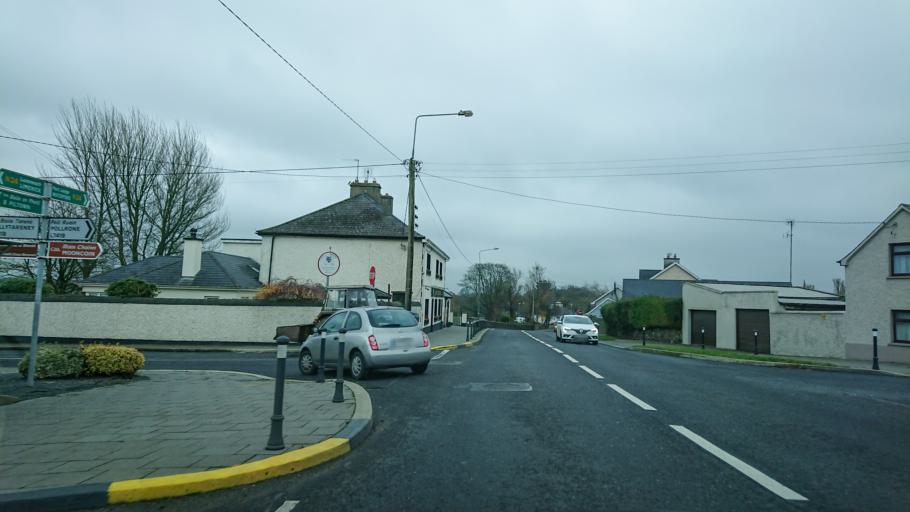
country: IE
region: Leinster
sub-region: Kilkenny
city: Mooncoin
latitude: 52.2957
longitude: -7.2597
